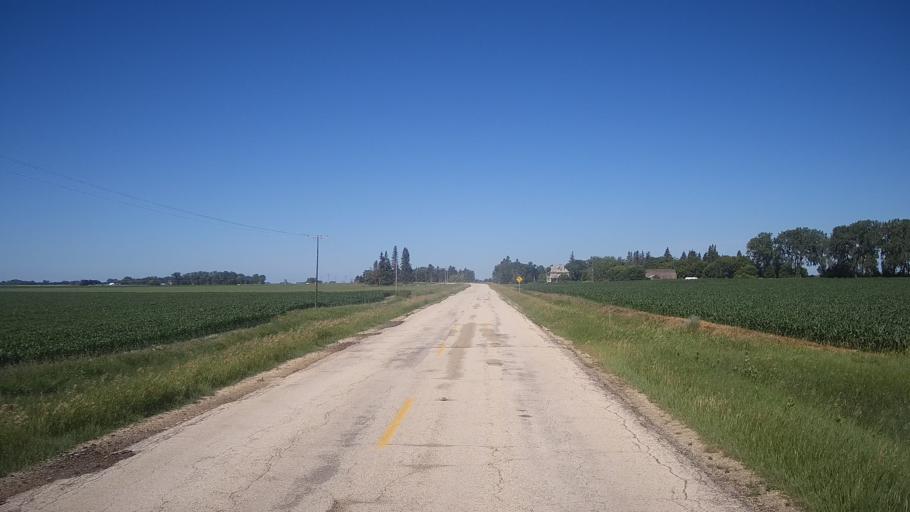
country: CA
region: Manitoba
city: Portage la Prairie
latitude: 50.0437
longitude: -98.0509
